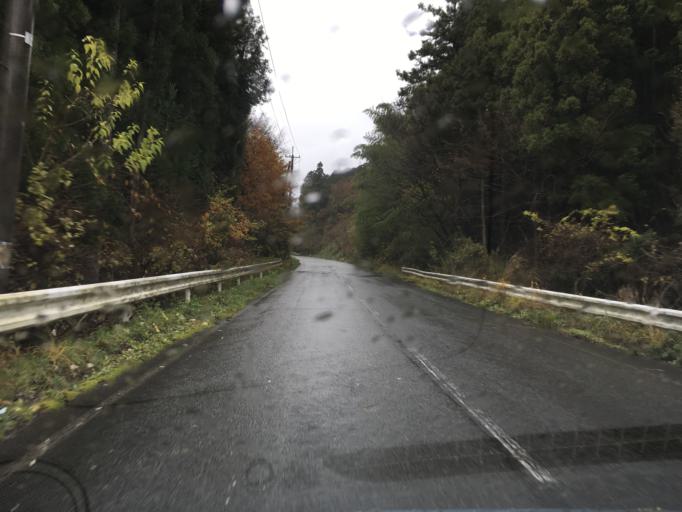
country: JP
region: Iwate
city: Ichinoseki
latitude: 38.7933
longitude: 141.2398
